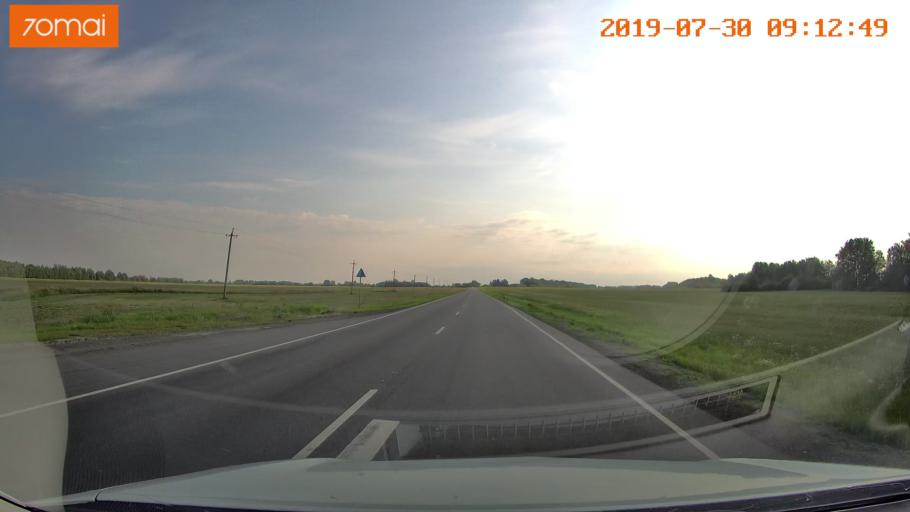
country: RU
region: Kaliningrad
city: Nesterov
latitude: 54.6197
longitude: 22.4840
